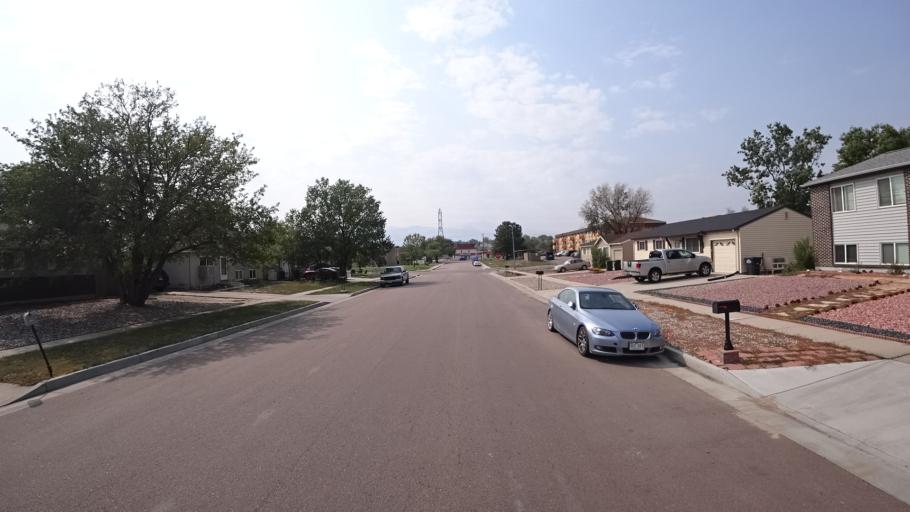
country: US
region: Colorado
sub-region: El Paso County
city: Stratmoor
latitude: 38.8286
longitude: -104.7552
